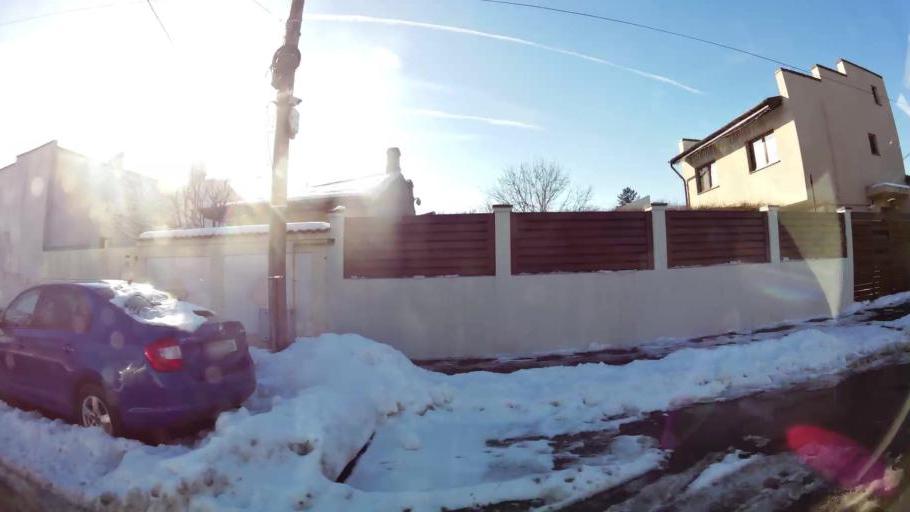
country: RO
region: Ilfov
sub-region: Comuna Fundeni-Dobroesti
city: Fundeni
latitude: 44.4739
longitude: 26.1444
